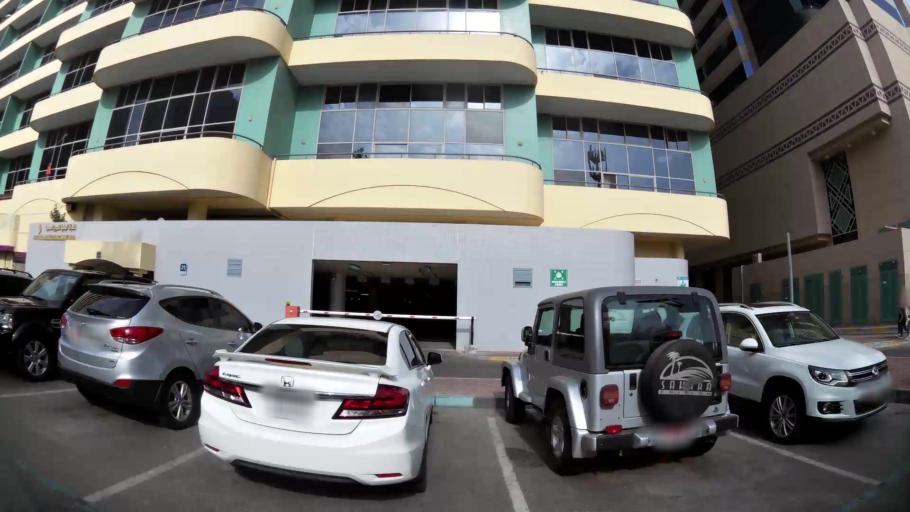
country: AE
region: Abu Dhabi
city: Abu Dhabi
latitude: 24.4751
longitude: 54.3464
